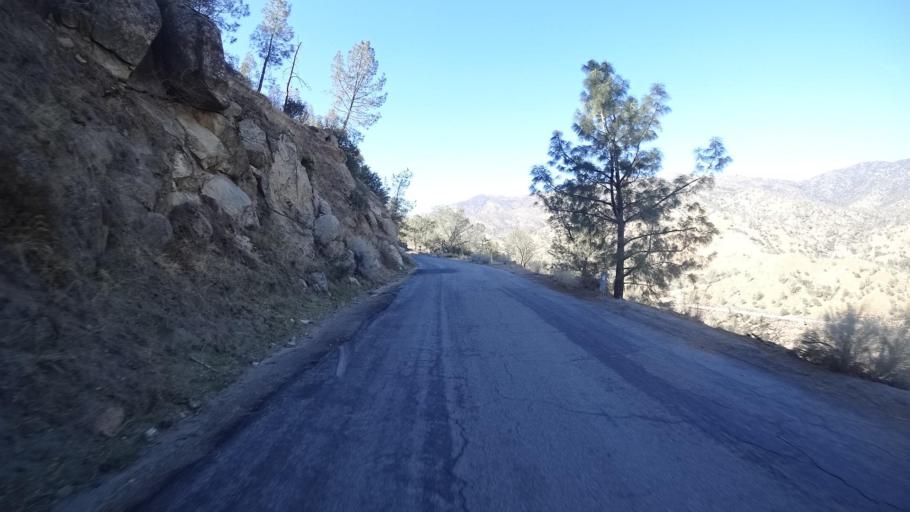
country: US
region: California
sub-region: Kern County
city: Bodfish
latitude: 35.5545
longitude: -118.6074
